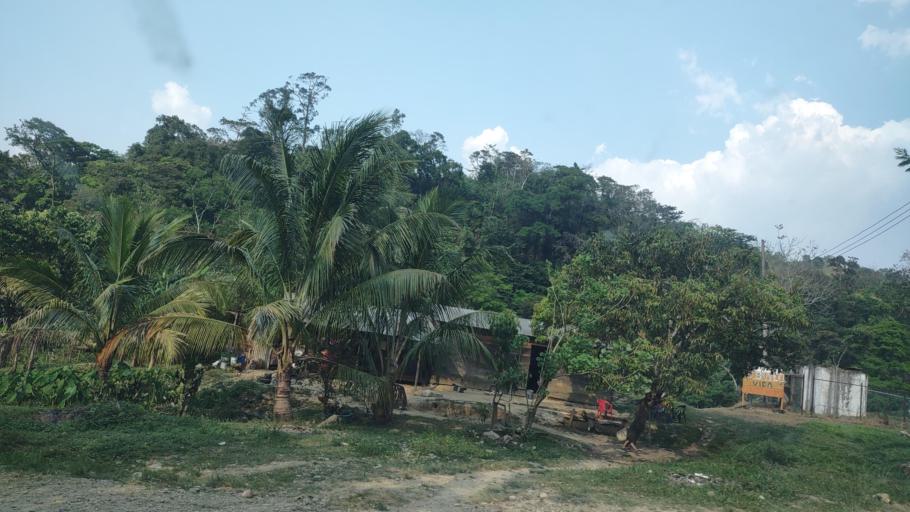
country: MX
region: Chiapas
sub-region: Tecpatan
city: Raudales Malpaso
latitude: 17.3090
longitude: -93.7781
